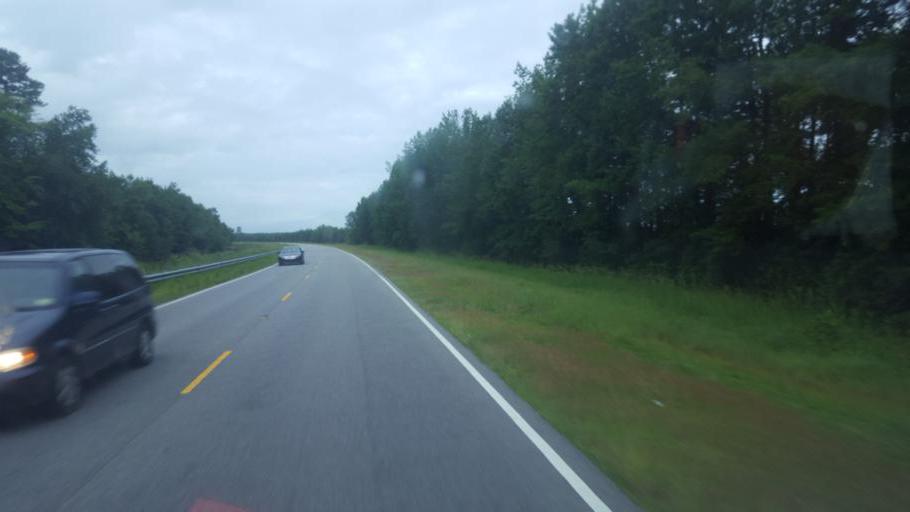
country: US
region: North Carolina
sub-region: Tyrrell County
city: Columbia
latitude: 35.9324
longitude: -76.1496
